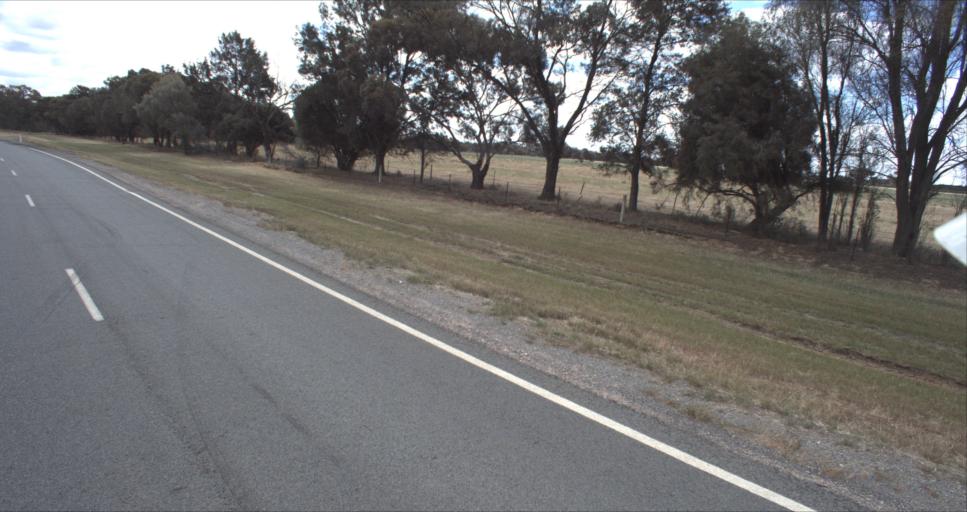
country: AU
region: New South Wales
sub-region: Leeton
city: Leeton
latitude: -34.6239
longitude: 146.3867
